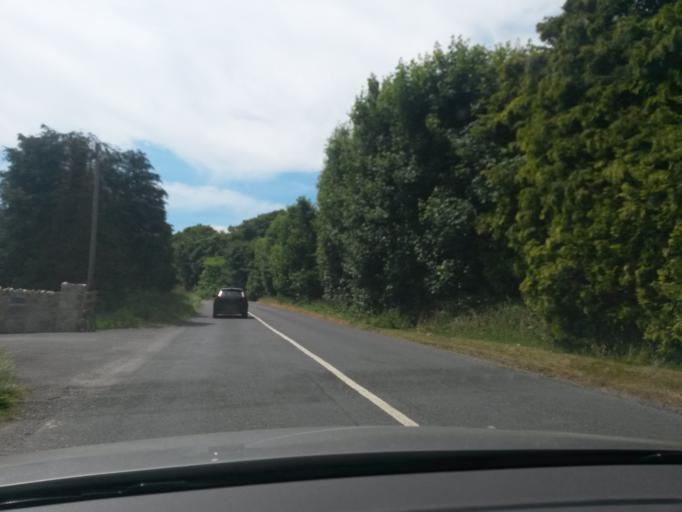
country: IE
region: Leinster
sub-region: Wicklow
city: Enniskerry
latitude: 53.1903
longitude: -6.2049
